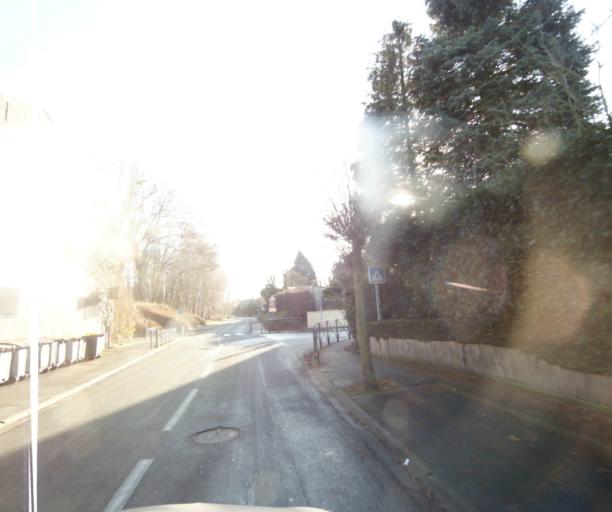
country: FR
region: Nord-Pas-de-Calais
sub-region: Departement du Nord
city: Saultain
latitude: 50.3359
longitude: 3.5744
